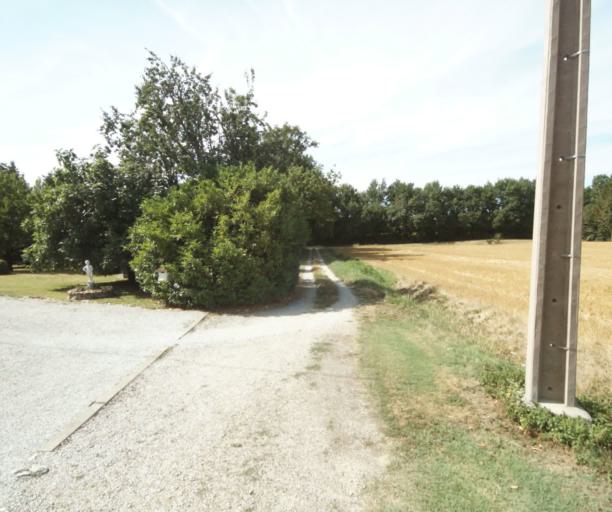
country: FR
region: Midi-Pyrenees
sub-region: Departement du Tarn
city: Soual
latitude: 43.5181
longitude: 2.0832
